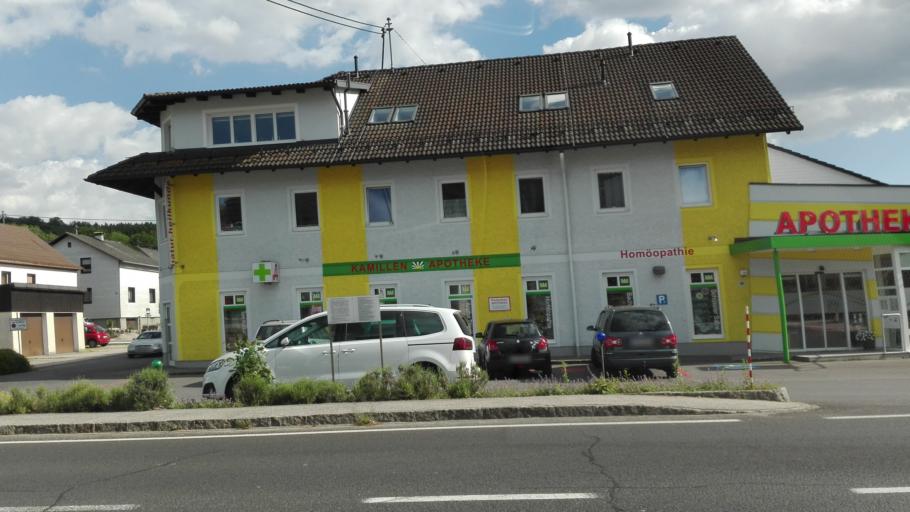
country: AT
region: Upper Austria
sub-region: Politischer Bezirk Urfahr-Umgebung
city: Altenberg bei Linz
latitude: 48.3372
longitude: 14.3673
